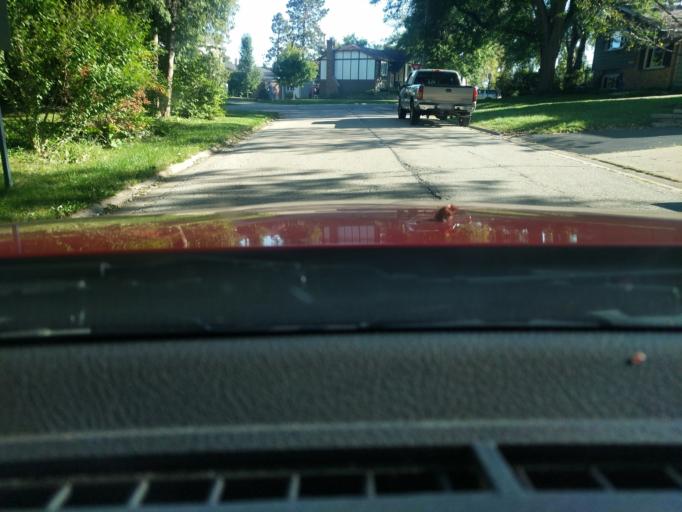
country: US
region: Illinois
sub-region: Lake County
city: Mundelein
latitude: 42.2744
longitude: -88.0022
